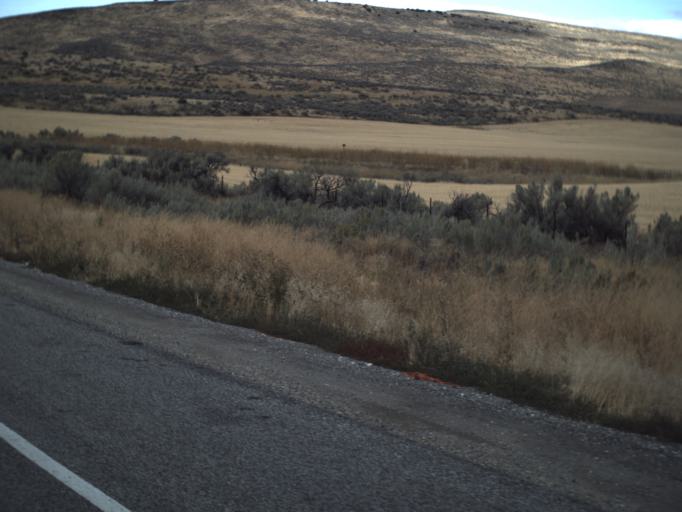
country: US
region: Utah
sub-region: Box Elder County
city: Garland
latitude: 41.8977
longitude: -112.5428
